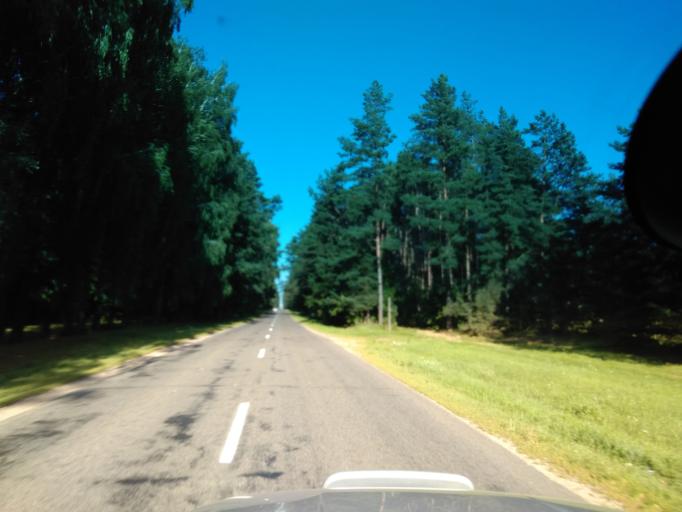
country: BY
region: Minsk
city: Uzda
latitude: 53.4591
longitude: 27.1673
